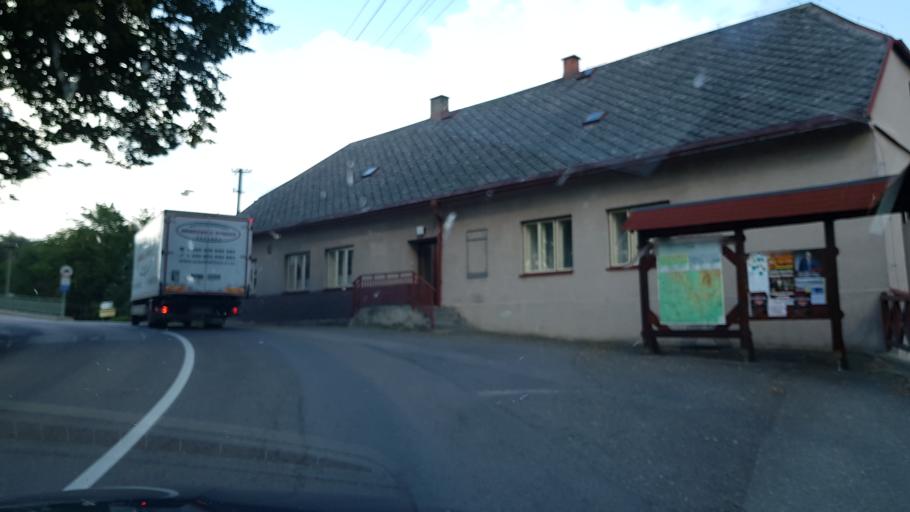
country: CZ
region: Pardubicky
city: Lukavice
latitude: 50.0795
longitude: 16.5086
